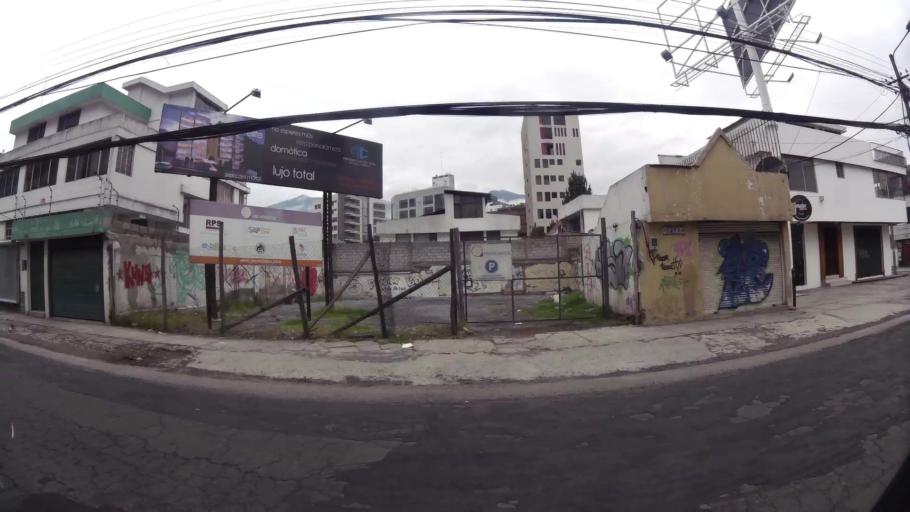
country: EC
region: Pichincha
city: Quito
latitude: -0.1916
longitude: -78.4823
